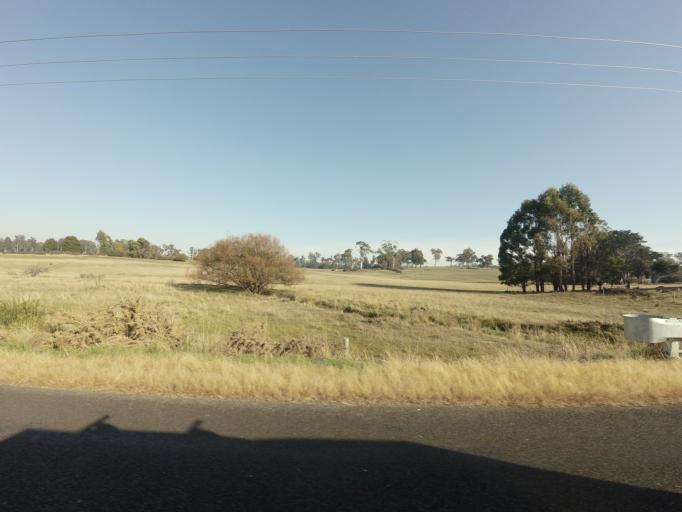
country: AU
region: Tasmania
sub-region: Northern Midlands
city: Longford
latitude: -41.5423
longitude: 146.9917
